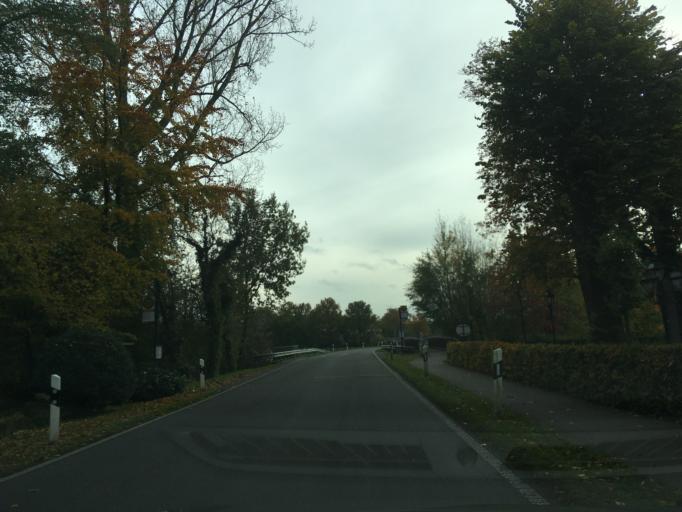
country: DE
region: North Rhine-Westphalia
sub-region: Regierungsbezirk Munster
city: Vreden
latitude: 52.0462
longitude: 6.8581
